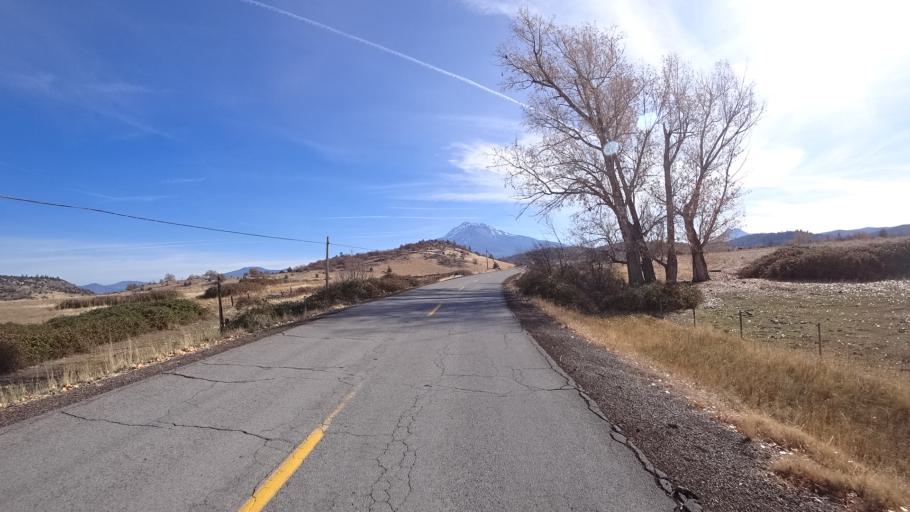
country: US
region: California
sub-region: Siskiyou County
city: Weed
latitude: 41.4708
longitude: -122.4382
